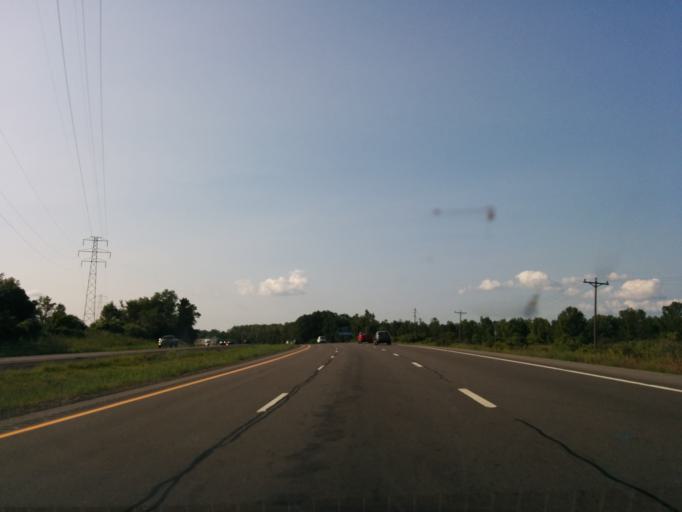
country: US
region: New York
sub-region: Onondaga County
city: North Syracuse
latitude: 43.1669
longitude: -76.1112
